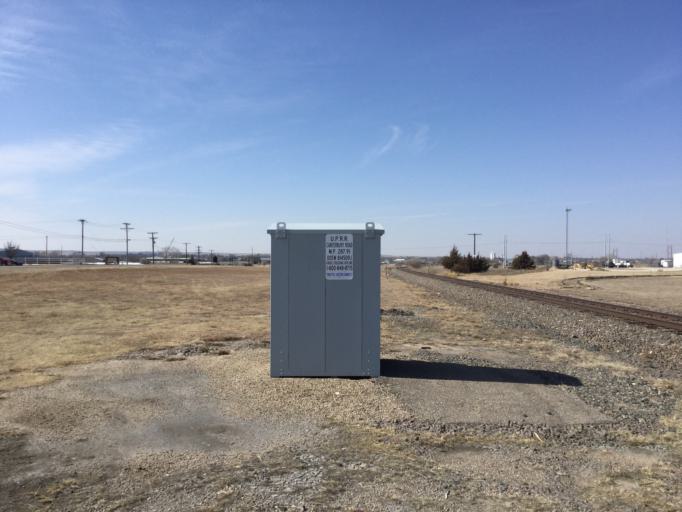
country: US
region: Kansas
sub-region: Ellis County
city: Hays
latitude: 38.8595
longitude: -99.2996
